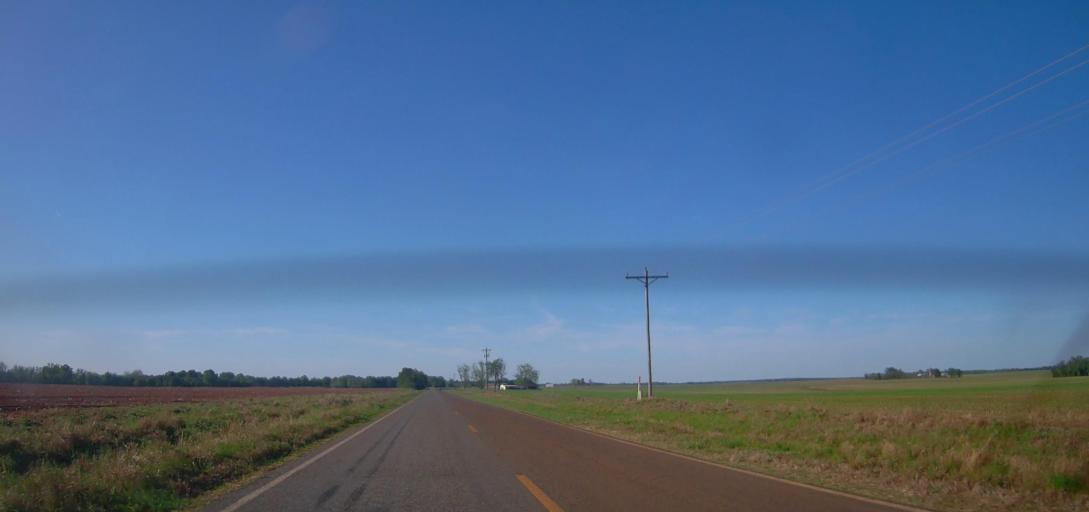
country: US
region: Georgia
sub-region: Macon County
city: Montezuma
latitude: 32.3436
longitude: -83.9438
